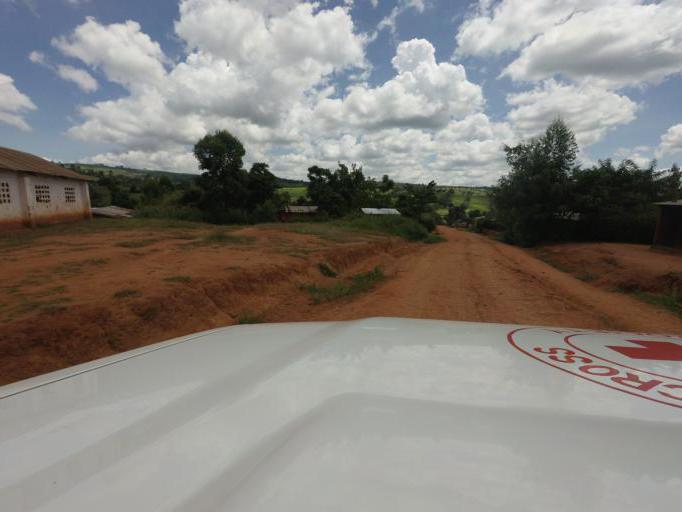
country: MW
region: Southern Region
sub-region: Thyolo District
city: Thyolo
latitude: -16.0354
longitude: 35.0553
